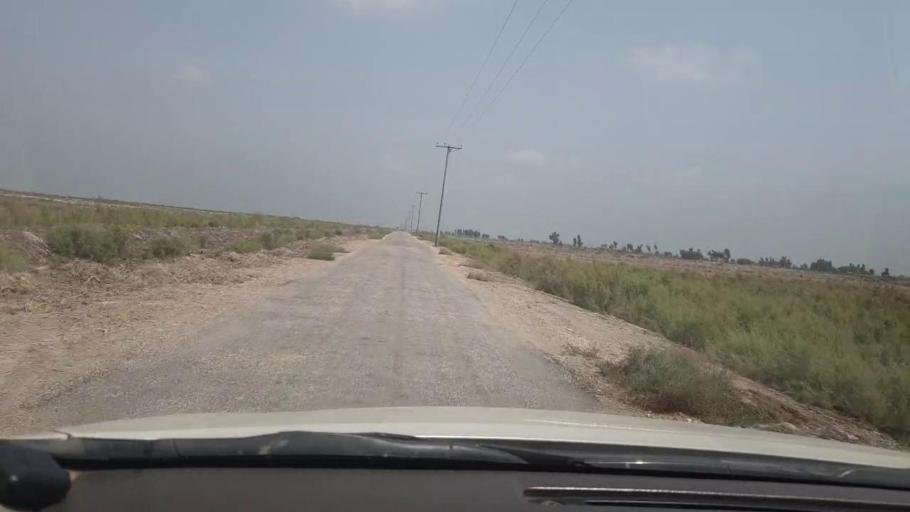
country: PK
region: Sindh
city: Garhi Yasin
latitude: 27.9917
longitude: 68.5014
